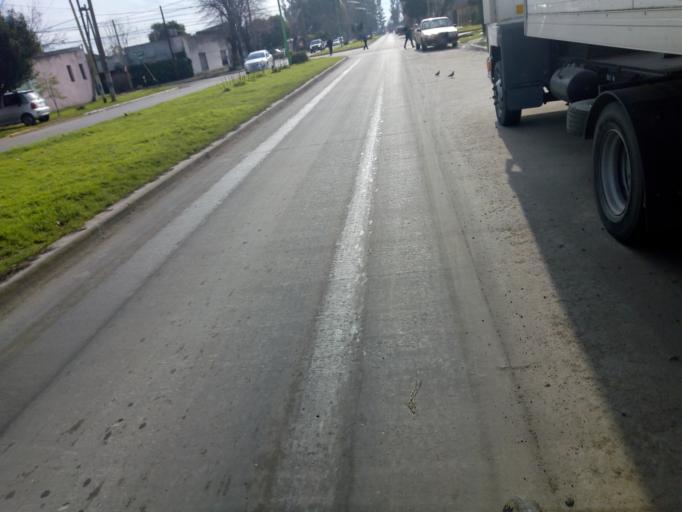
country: AR
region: Buenos Aires
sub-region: Partido de La Plata
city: La Plata
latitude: -34.8972
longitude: -57.9350
